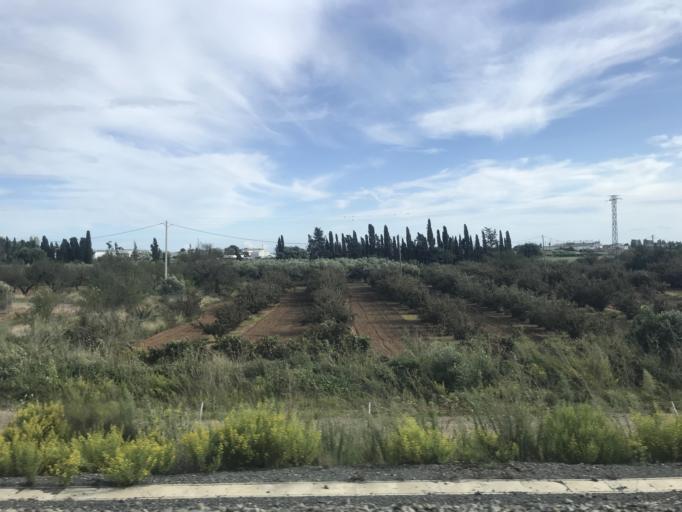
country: ES
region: Catalonia
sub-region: Provincia de Tarragona
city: Cambrils
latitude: 41.0969
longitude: 1.0893
